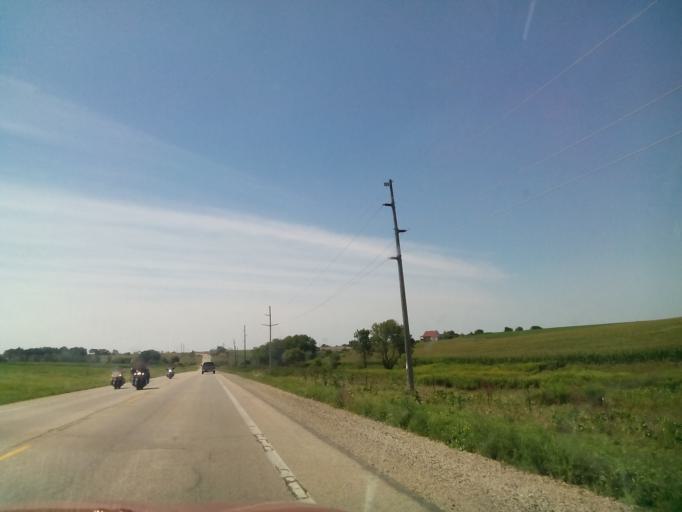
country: US
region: Wisconsin
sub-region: Green County
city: Monroe
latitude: 42.6640
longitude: -89.6229
